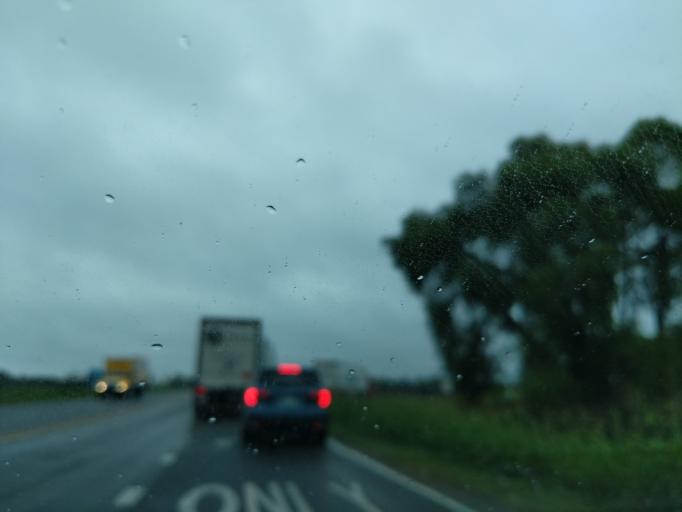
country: US
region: Louisiana
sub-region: Caddo Parish
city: Greenwood
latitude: 32.4443
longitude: -93.9813
